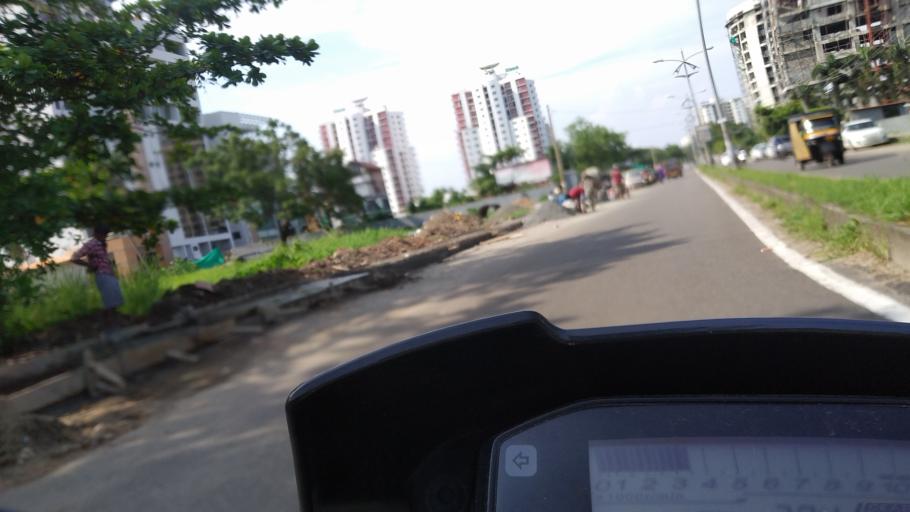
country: IN
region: Kerala
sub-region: Ernakulam
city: Cochin
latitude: 9.9879
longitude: 76.3020
